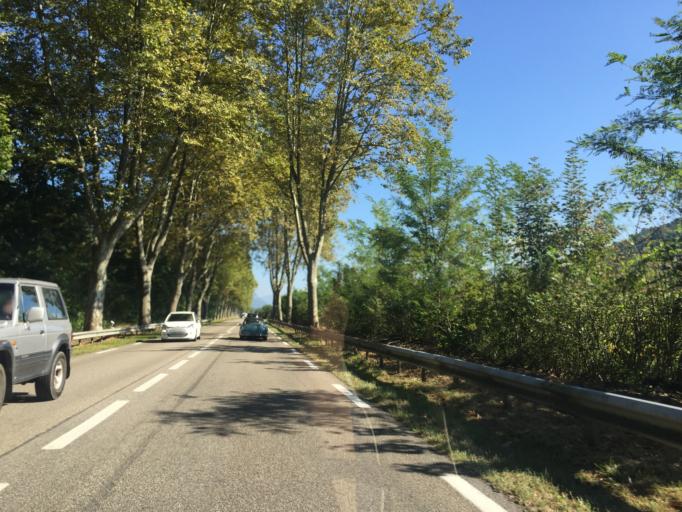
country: FR
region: Rhone-Alpes
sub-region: Departement de la Savoie
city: Cruet
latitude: 45.5236
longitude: 6.1076
